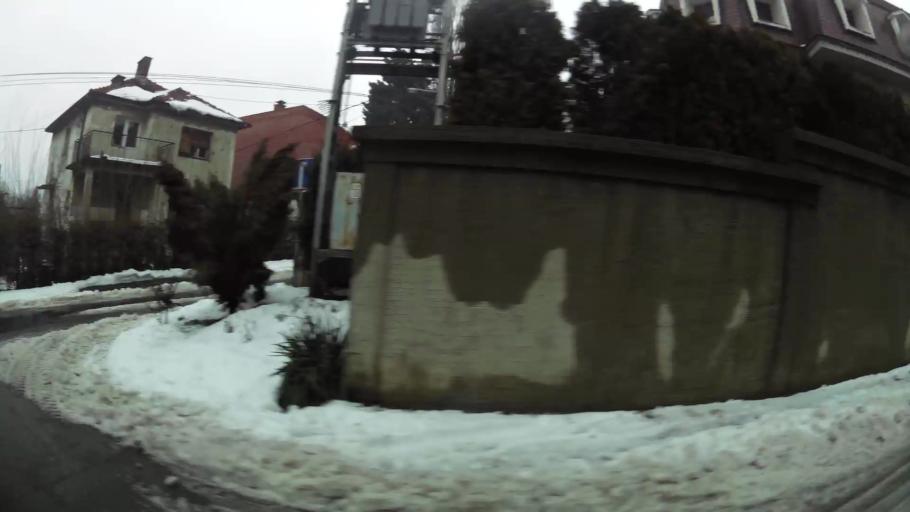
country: RS
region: Central Serbia
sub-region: Belgrade
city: Zvezdara
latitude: 44.7864
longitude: 20.5206
